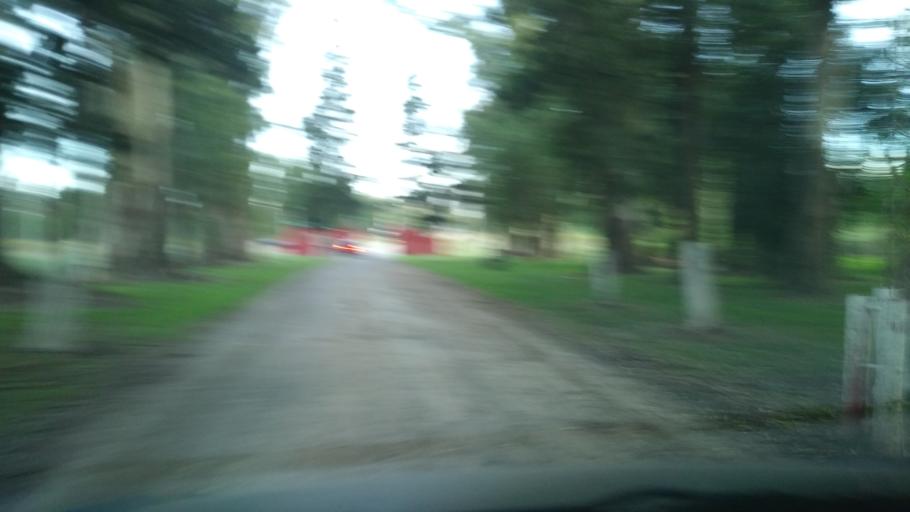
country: AR
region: Buenos Aires
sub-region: Partido de Lujan
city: Lujan
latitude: -34.5926
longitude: -59.1505
